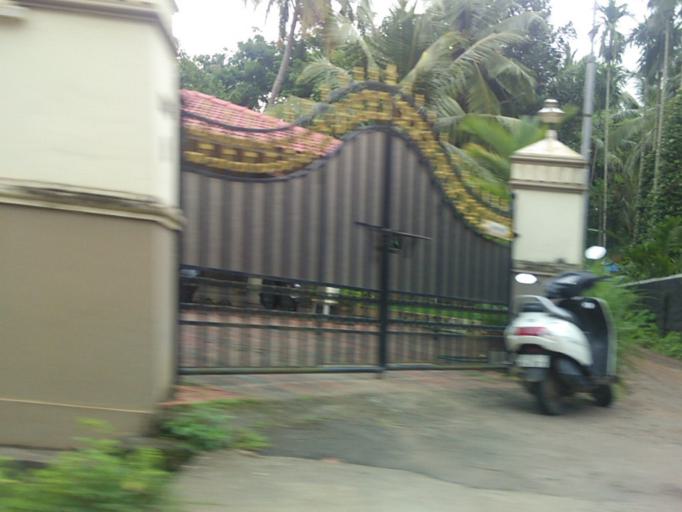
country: IN
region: Kerala
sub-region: Kozhikode
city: Kozhikode
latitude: 11.2857
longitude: 75.8115
